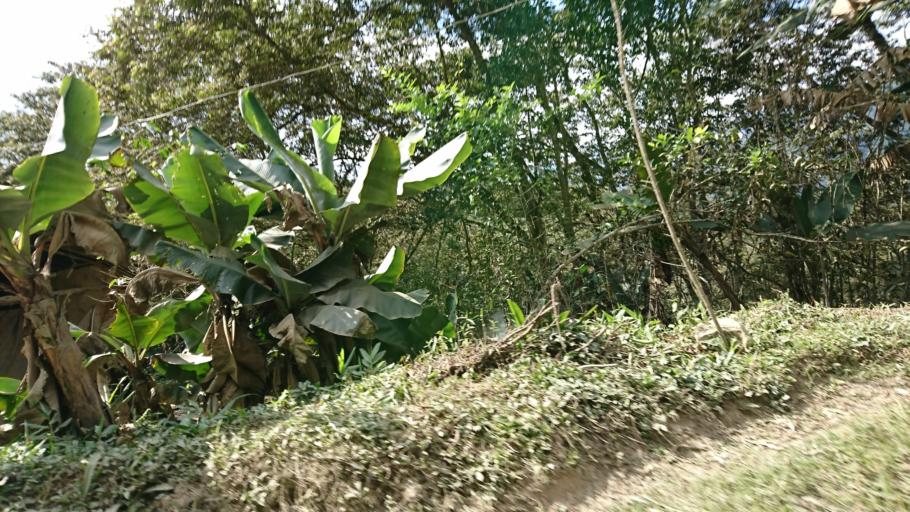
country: BO
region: La Paz
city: Coroico
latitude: -16.1150
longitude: -67.7655
